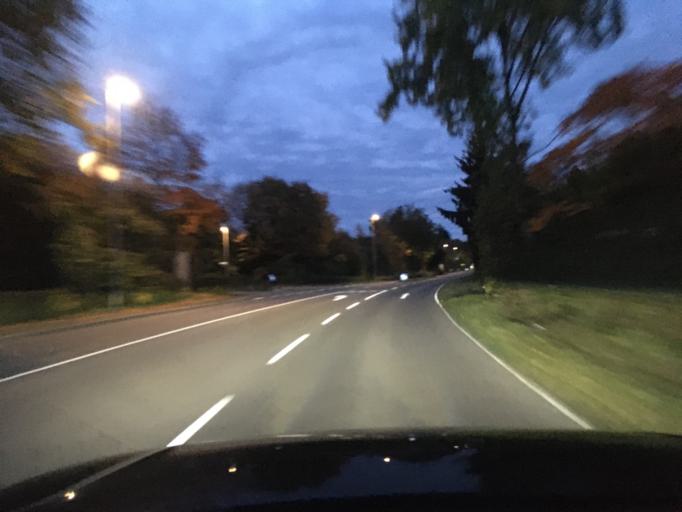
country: DE
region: Baden-Wuerttemberg
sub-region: Regierungsbezirk Stuttgart
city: Bad Wimpfen
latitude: 49.2245
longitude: 9.1607
